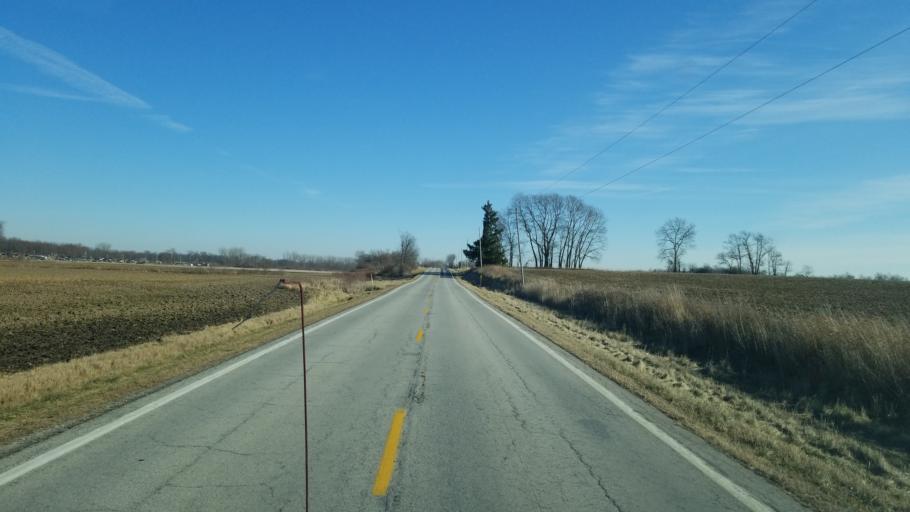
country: US
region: Ohio
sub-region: Henry County
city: Liberty Center
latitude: 41.4152
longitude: -83.9582
